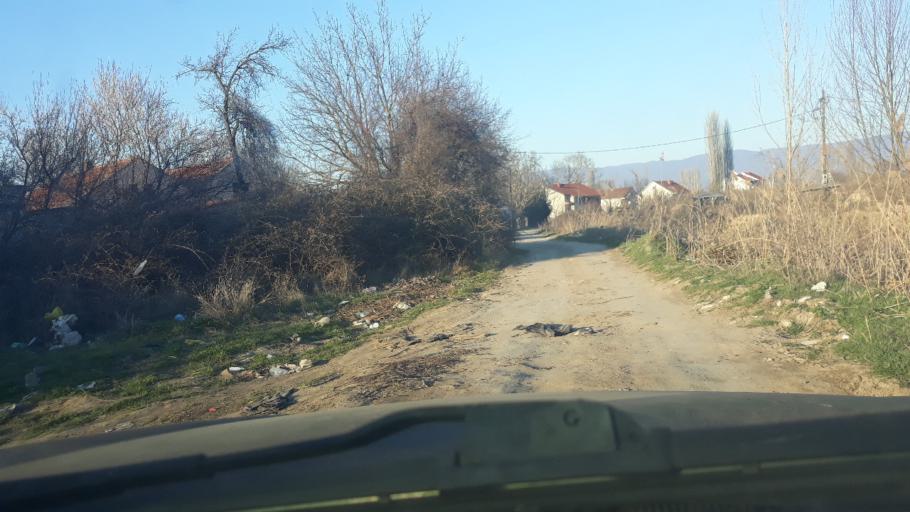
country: MK
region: Strumica
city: Strumica
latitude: 41.4446
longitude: 22.6278
